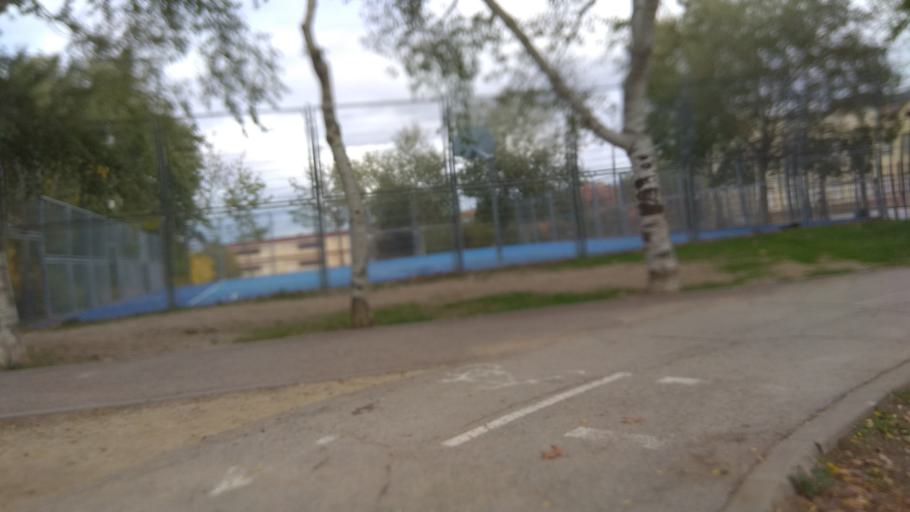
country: ES
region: Madrid
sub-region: Provincia de Madrid
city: Vicalvaro
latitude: 40.4091
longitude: -3.6155
